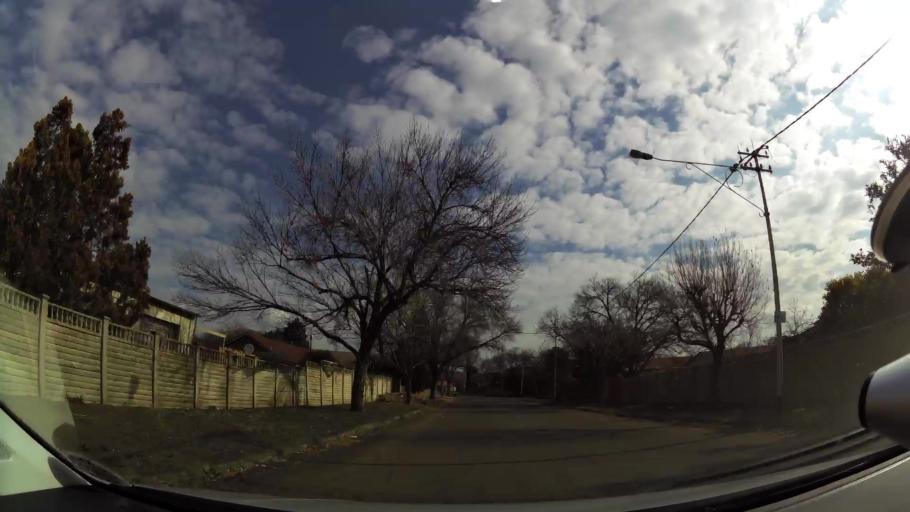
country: ZA
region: Orange Free State
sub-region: Mangaung Metropolitan Municipality
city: Bloemfontein
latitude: -29.0880
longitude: 26.2490
